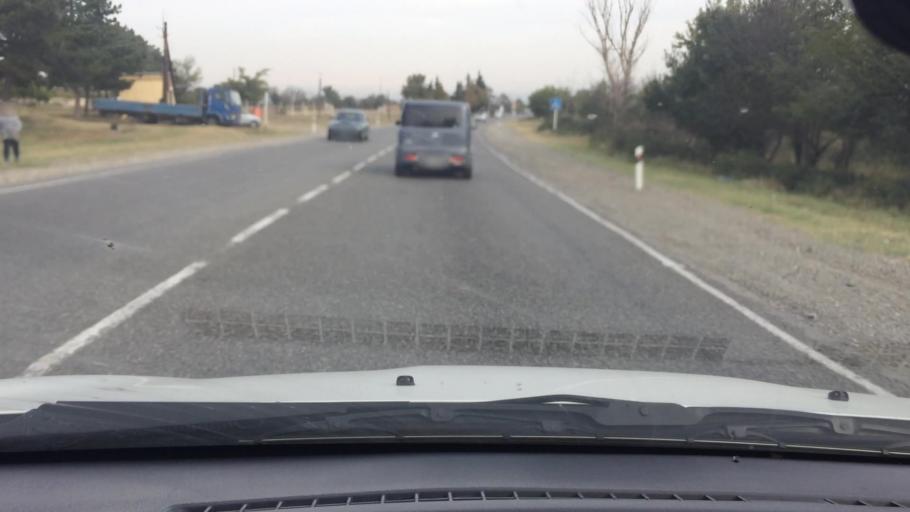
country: GE
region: T'bilisi
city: Tbilisi
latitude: 41.6437
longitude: 44.8508
